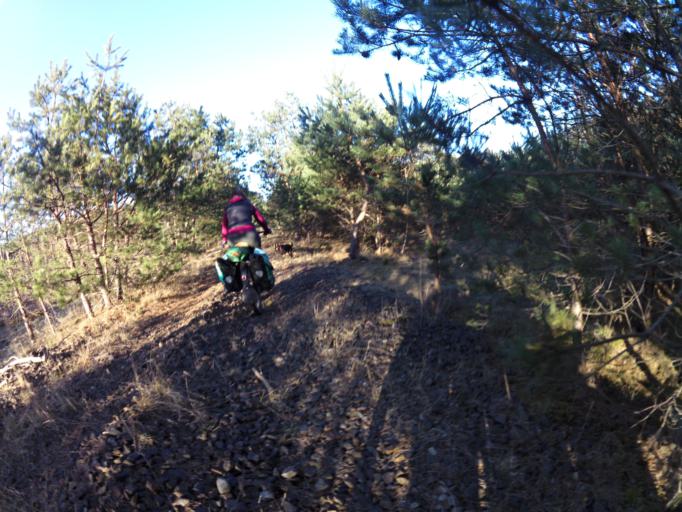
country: PL
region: West Pomeranian Voivodeship
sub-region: Powiat mysliborski
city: Debno
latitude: 52.8252
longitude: 14.7644
